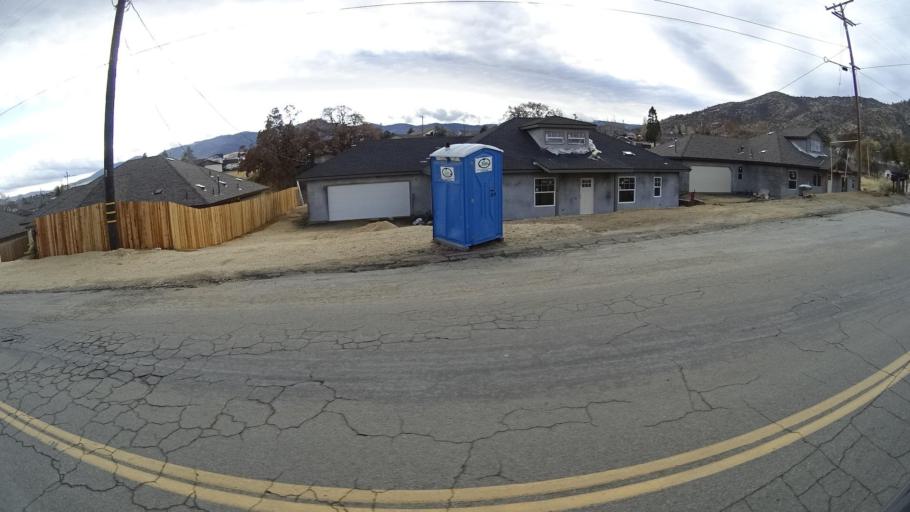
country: US
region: California
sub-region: Kern County
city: Golden Hills
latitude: 35.1540
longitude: -118.5031
